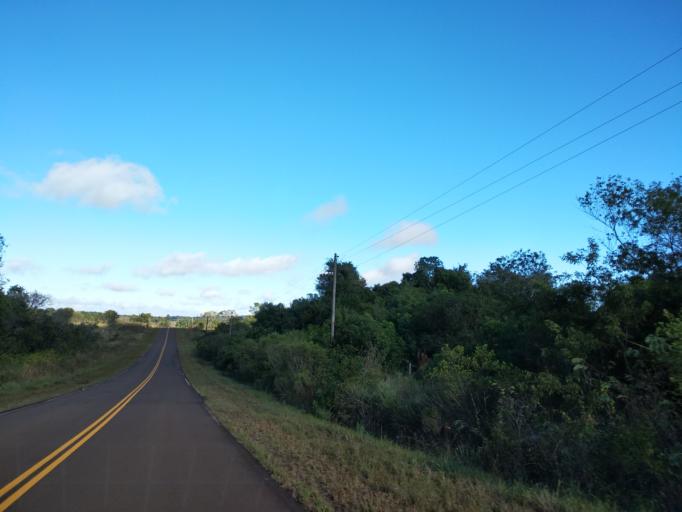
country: AR
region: Misiones
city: Santa Ana
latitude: -27.4099
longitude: -55.5557
